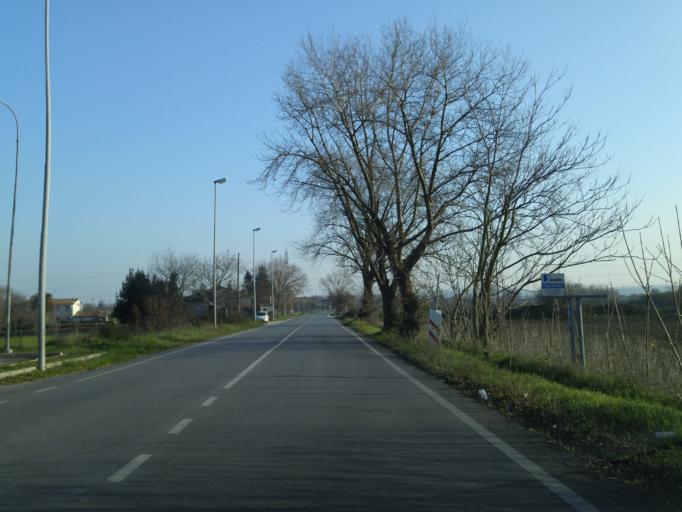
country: IT
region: The Marches
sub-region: Provincia di Pesaro e Urbino
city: Rosciano
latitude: 43.8077
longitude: 12.9831
